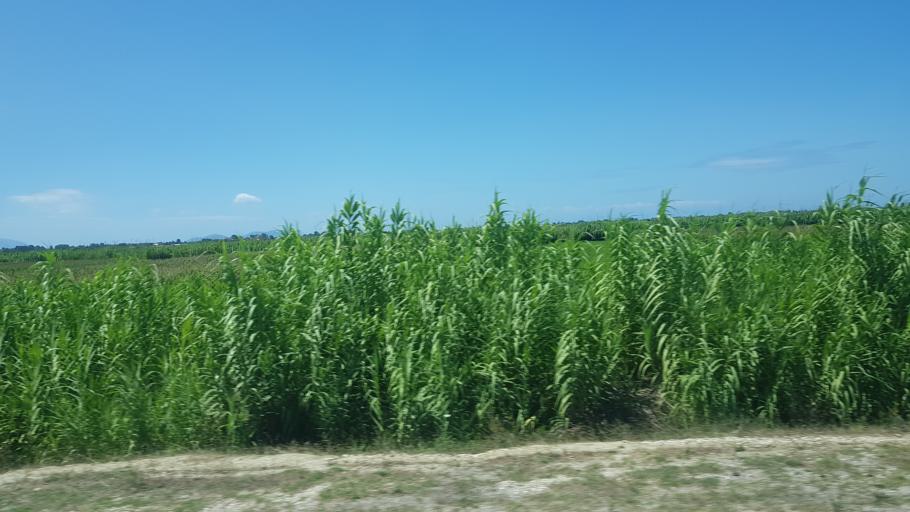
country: AL
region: Fier
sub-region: Rrethi i Fierit
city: Frakulla e Madhe
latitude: 40.6518
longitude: 19.4941
